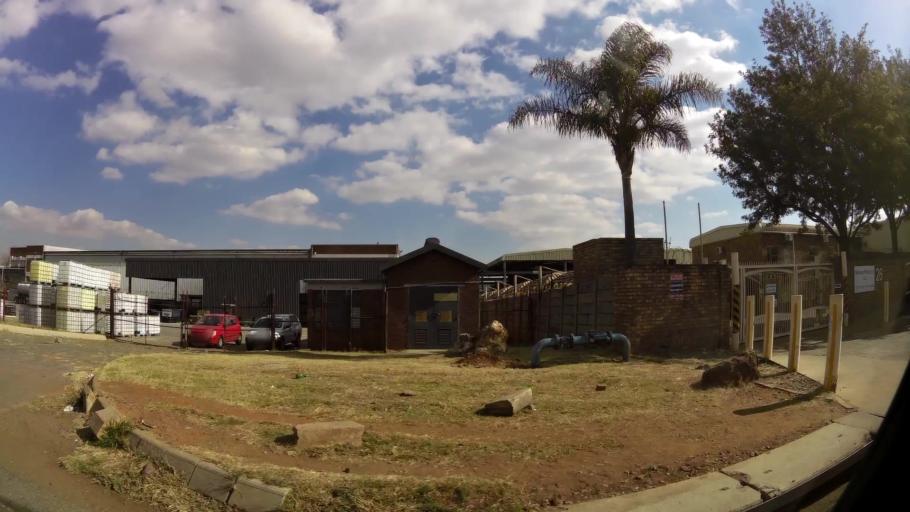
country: ZA
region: Gauteng
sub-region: Ekurhuleni Metropolitan Municipality
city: Tembisa
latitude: -25.9676
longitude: 28.2339
